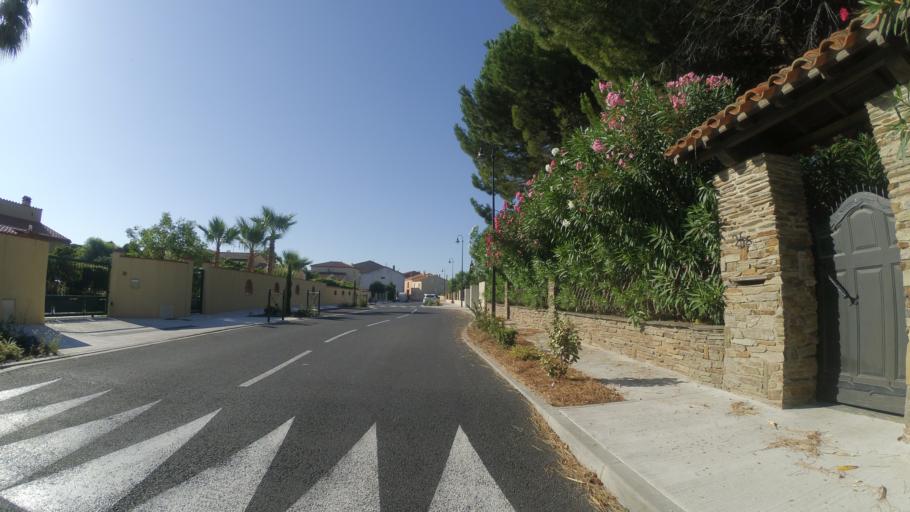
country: FR
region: Languedoc-Roussillon
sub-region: Departement des Pyrenees-Orientales
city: Villeneuve-la-Riviere
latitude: 42.6956
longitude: 2.8002
